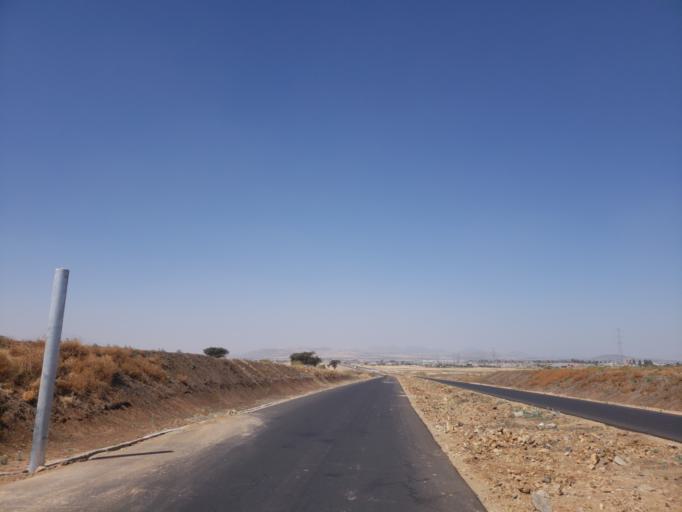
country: ET
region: Oromiya
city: Mojo
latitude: 8.5657
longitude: 39.1529
